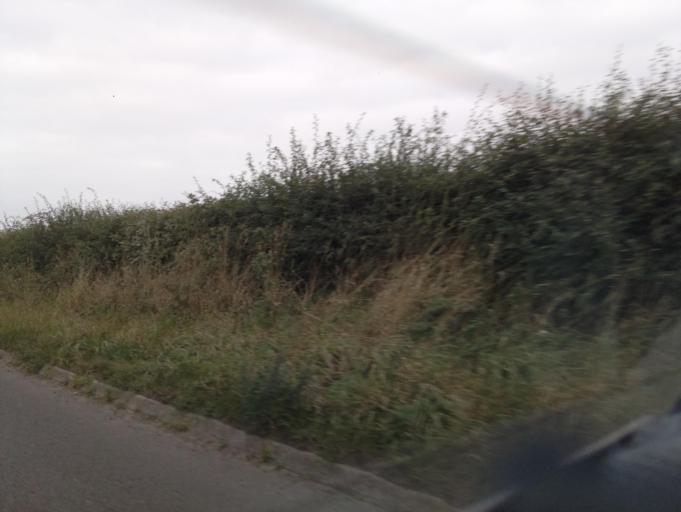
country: GB
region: England
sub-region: Shropshire
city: Shawbury
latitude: 52.8184
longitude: -2.6099
